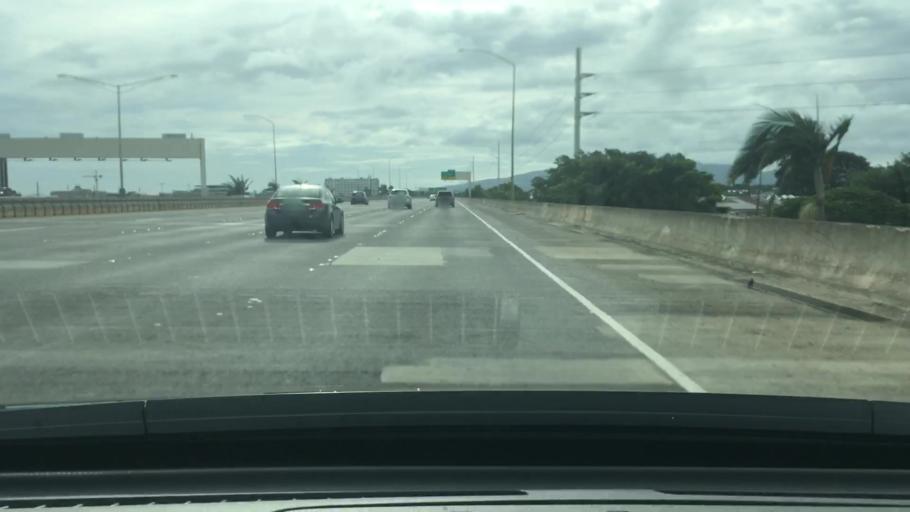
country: US
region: Hawaii
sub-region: Honolulu County
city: Halawa Heights
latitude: 21.3356
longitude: -157.9024
